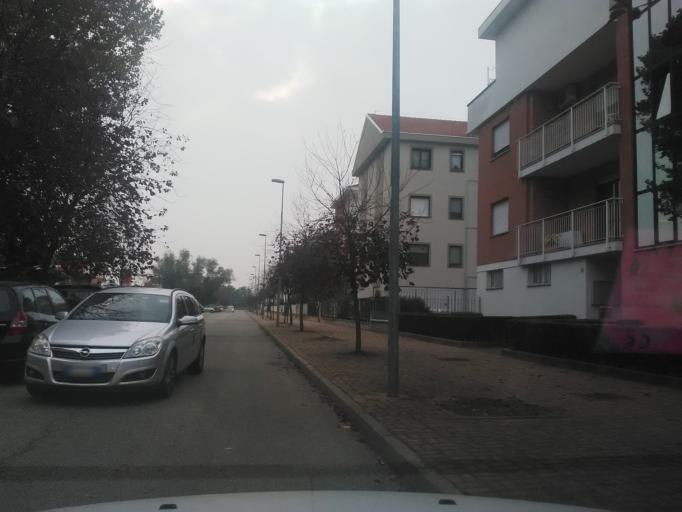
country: IT
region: Piedmont
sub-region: Provincia di Vercelli
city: Vercelli
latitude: 45.3265
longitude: 8.4007
